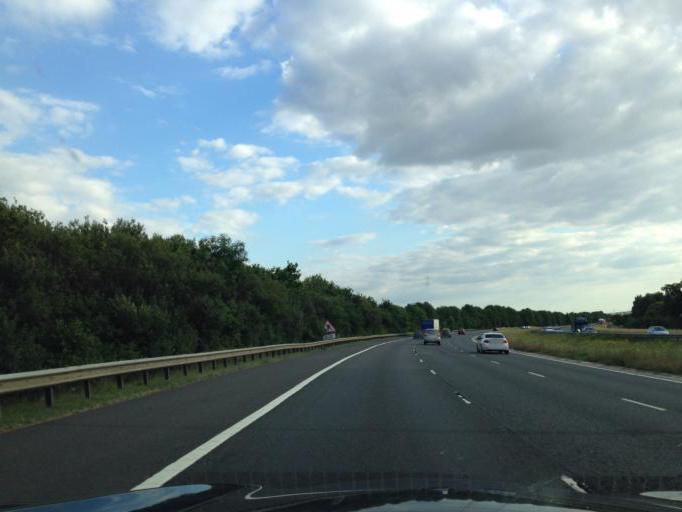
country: GB
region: England
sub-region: Oxfordshire
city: Wheatley
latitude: 51.7905
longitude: -1.0857
